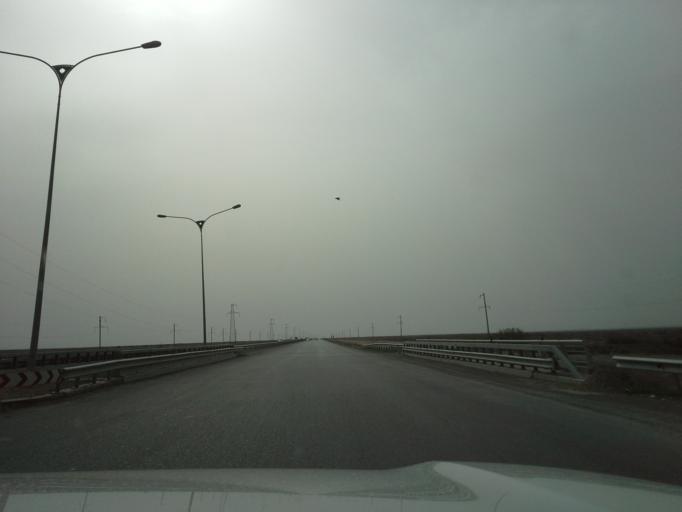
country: TM
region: Ahal
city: Kaka
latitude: 37.5344
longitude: 59.4091
